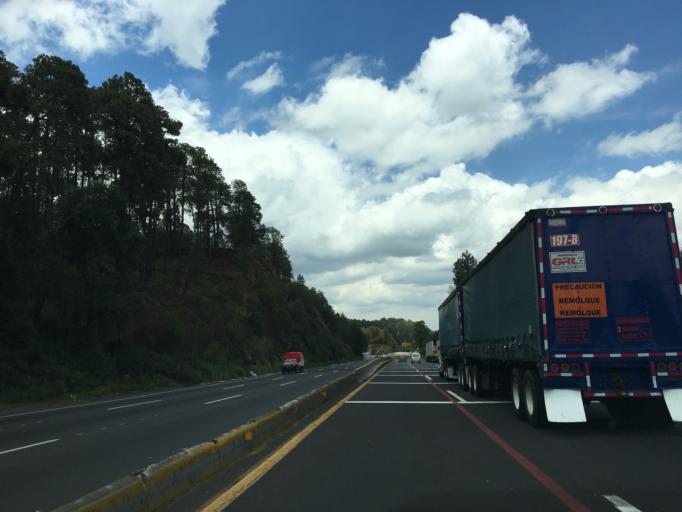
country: MX
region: Mexico
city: Rio Frio de Juarez
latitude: 19.3093
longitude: -98.7457
